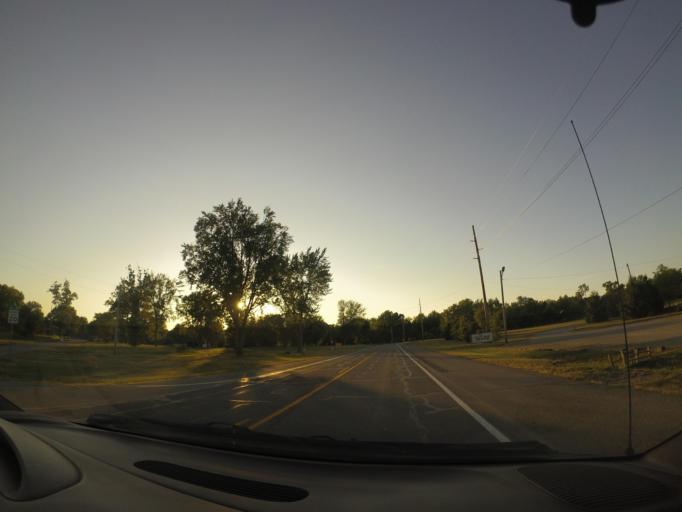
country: US
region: Indiana
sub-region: Steuben County
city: Angola
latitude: 41.6429
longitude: -85.1613
